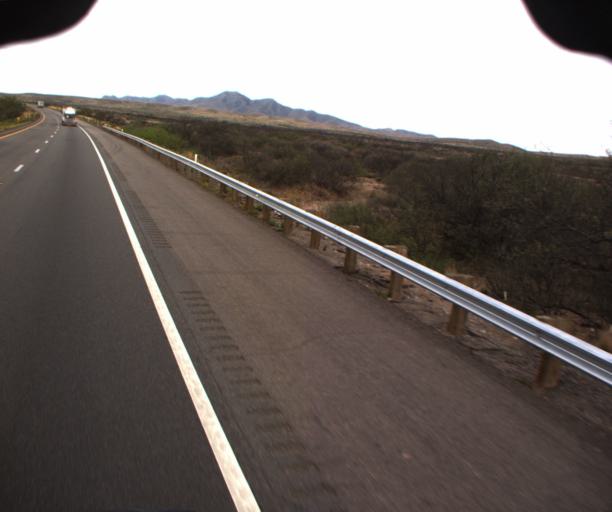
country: US
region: Arizona
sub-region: Cochise County
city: Willcox
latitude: 32.1526
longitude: -109.9898
